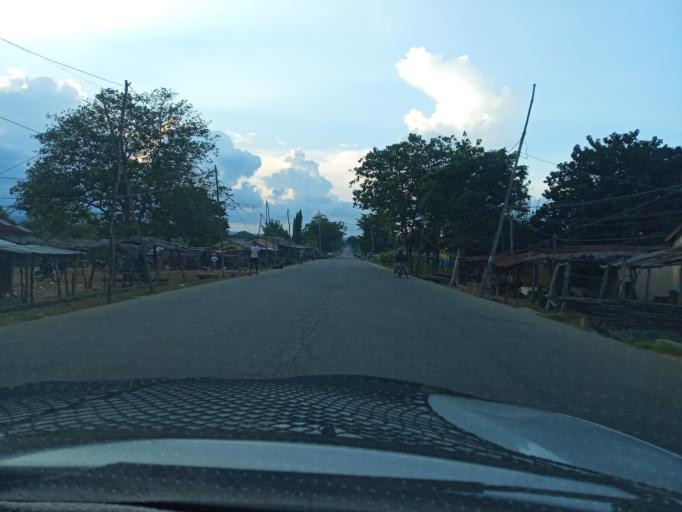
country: TG
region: Centrale
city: Sokode
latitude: 8.8363
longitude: 1.0777
